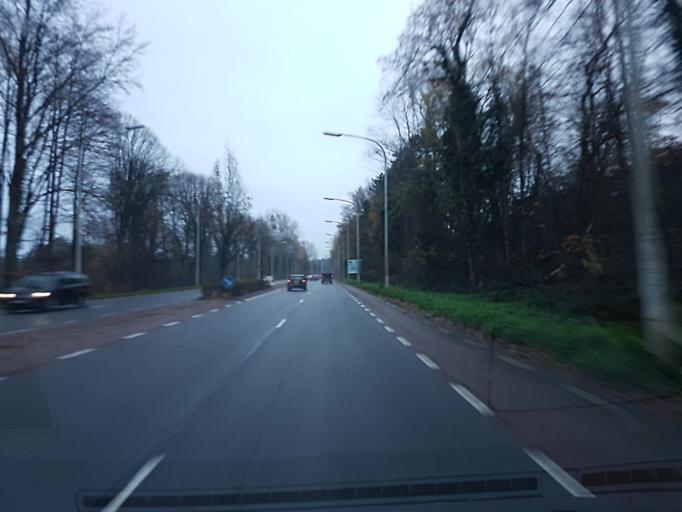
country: BE
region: Wallonia
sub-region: Province de Namur
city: Namur
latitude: 50.4586
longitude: 4.8912
